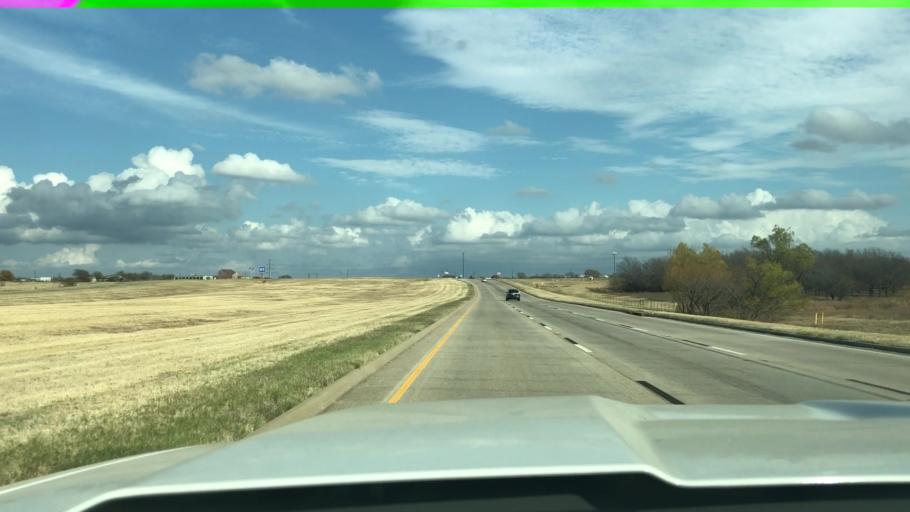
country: US
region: Texas
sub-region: Tarrant County
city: Keller
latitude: 32.9731
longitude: -97.2750
